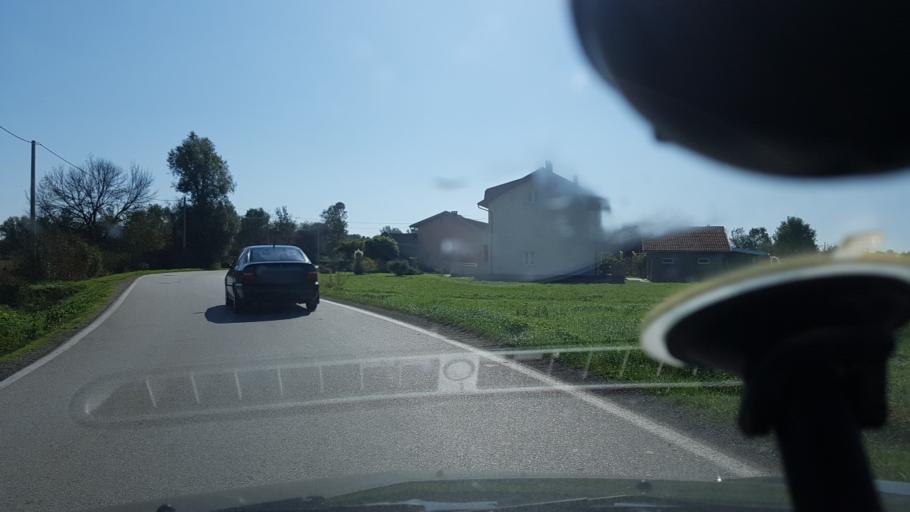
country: HR
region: Zagrebacka
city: Lupoglav
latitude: 45.7457
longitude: 16.3025
